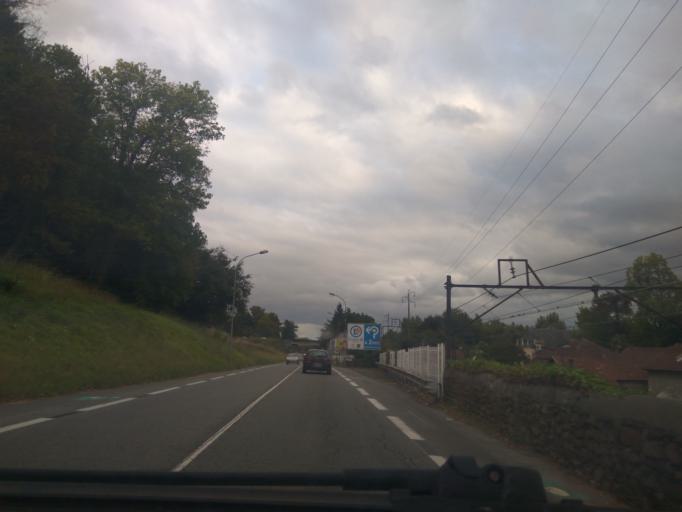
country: FR
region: Aquitaine
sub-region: Departement des Pyrenees-Atlantiques
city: Bizanos
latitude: 43.2866
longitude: -0.3500
